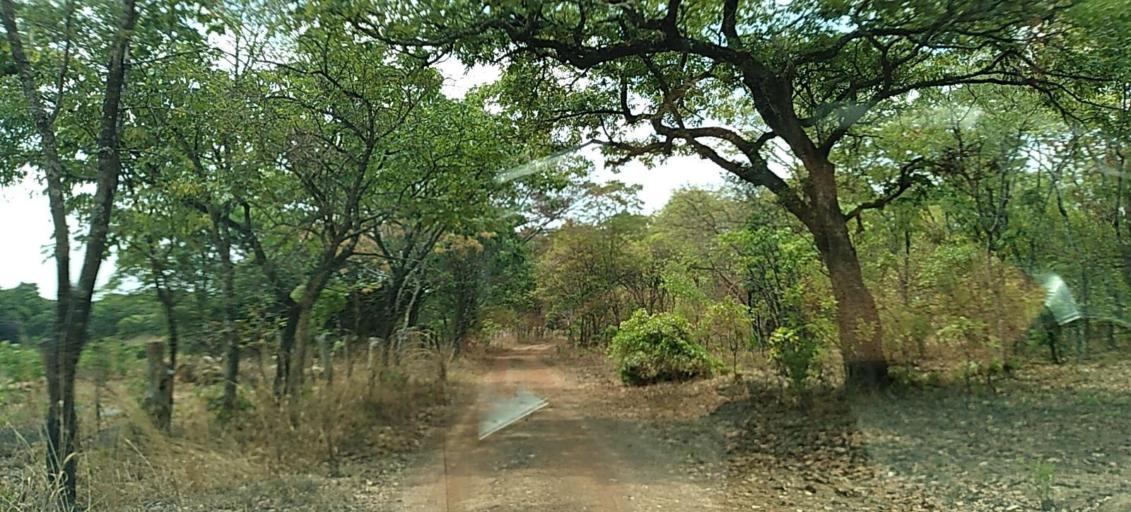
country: ZM
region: Copperbelt
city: Chililabombwe
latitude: -12.4600
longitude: 27.6457
